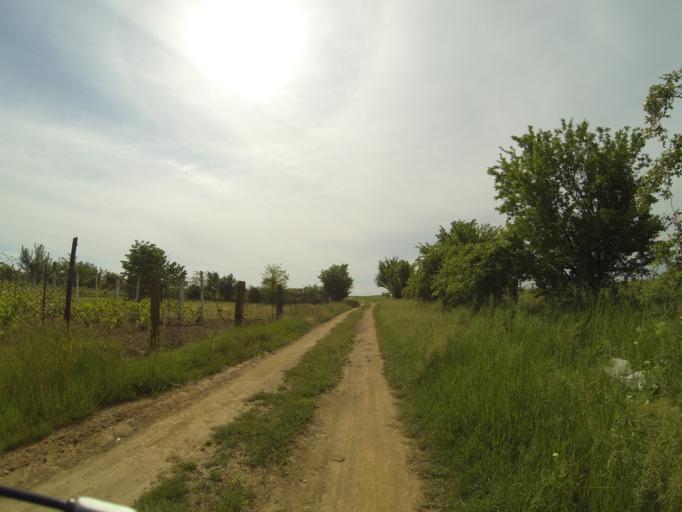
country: RO
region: Dolj
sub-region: Comuna Malu Mare
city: Preajba
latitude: 44.2621
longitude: 23.8600
